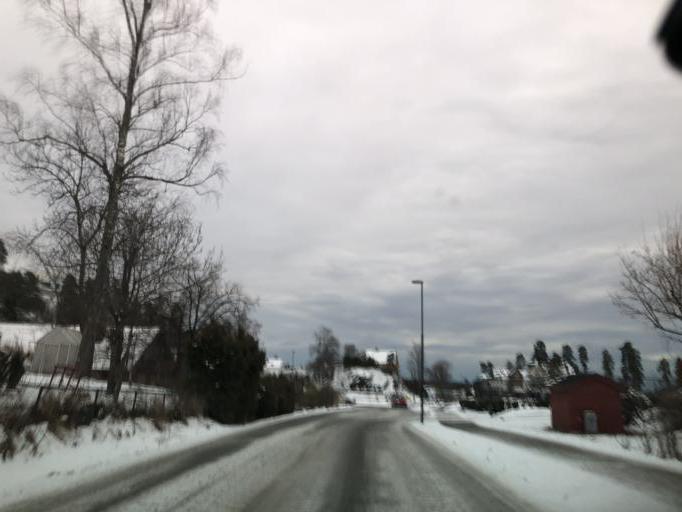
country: NO
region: Akershus
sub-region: Baerum
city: Sandvika
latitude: 59.8601
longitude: 10.5165
